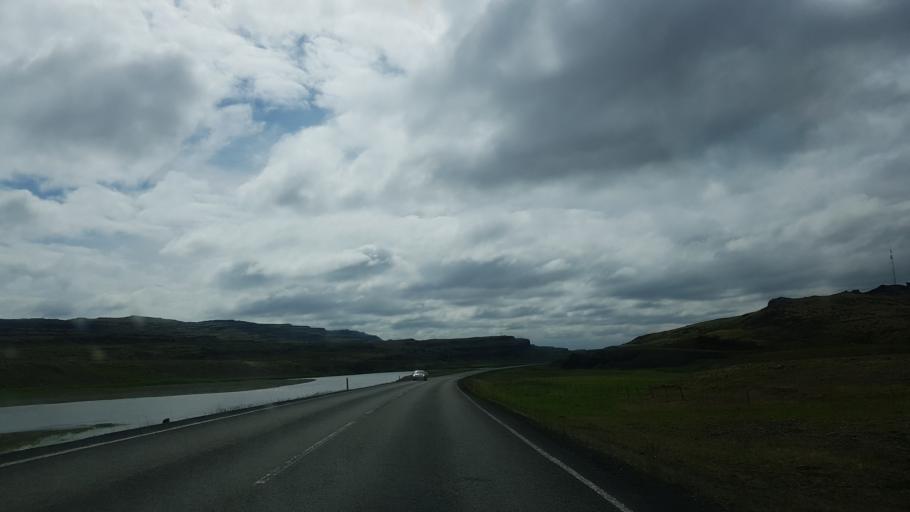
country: IS
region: West
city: Borgarnes
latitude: 64.8095
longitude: -21.4182
